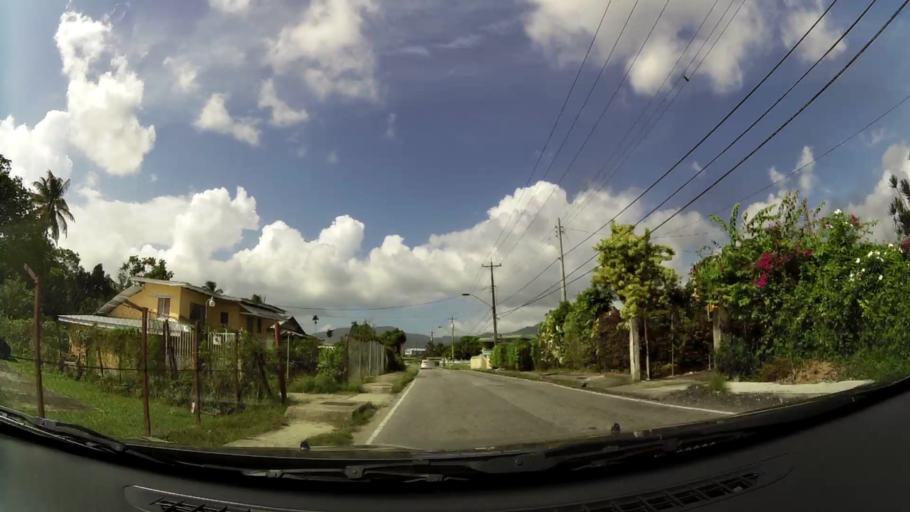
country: TT
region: Tunapuna/Piarco
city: Arouca
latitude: 10.6187
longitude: -61.3095
